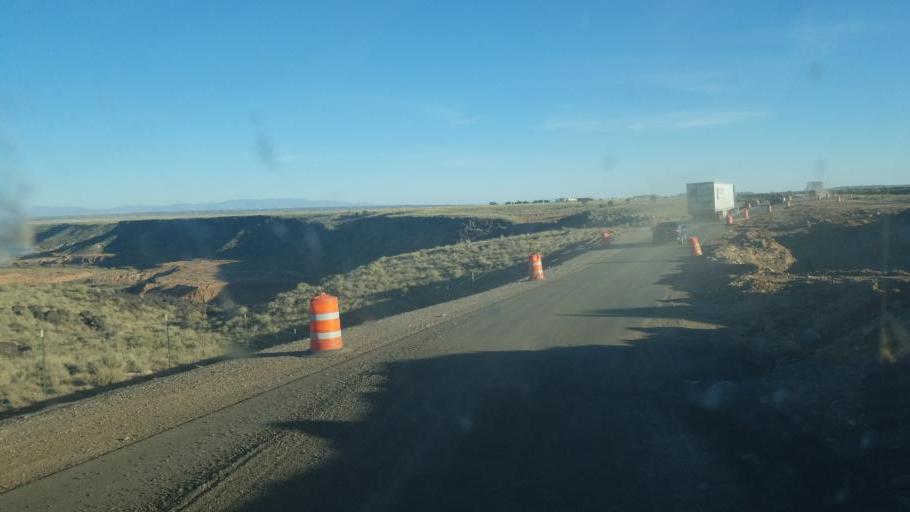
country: US
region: New Mexico
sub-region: Cibola County
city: Laguna
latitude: 34.8972
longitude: -107.0849
